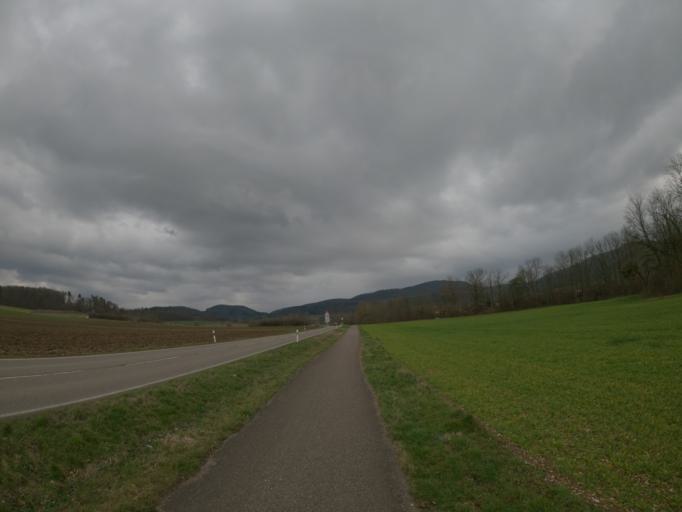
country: DE
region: Baden-Wuerttemberg
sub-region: Regierungsbezirk Stuttgart
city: Schlat
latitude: 48.6639
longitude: 9.7003
